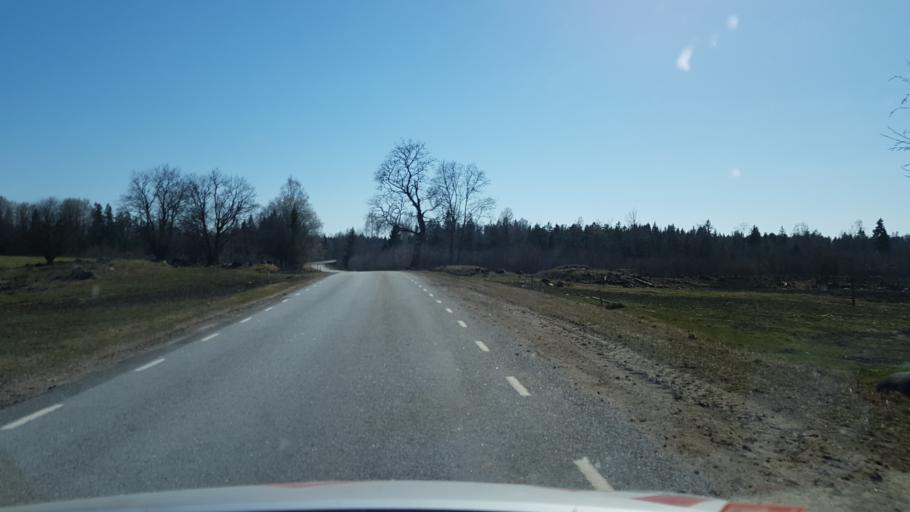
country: EE
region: Laeaene-Virumaa
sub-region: Tamsalu vald
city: Tamsalu
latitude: 59.0600
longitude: 26.1032
